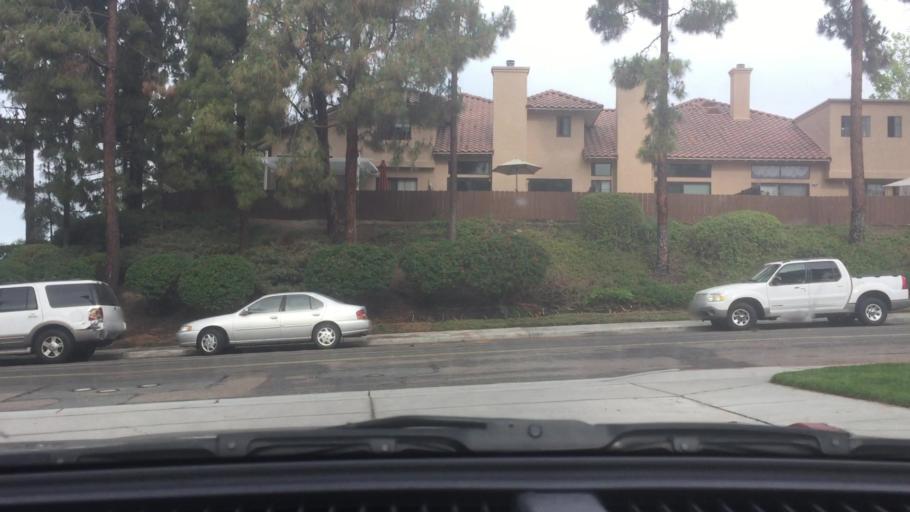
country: US
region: California
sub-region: San Diego County
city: Del Mar
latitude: 32.9404
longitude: -117.2327
